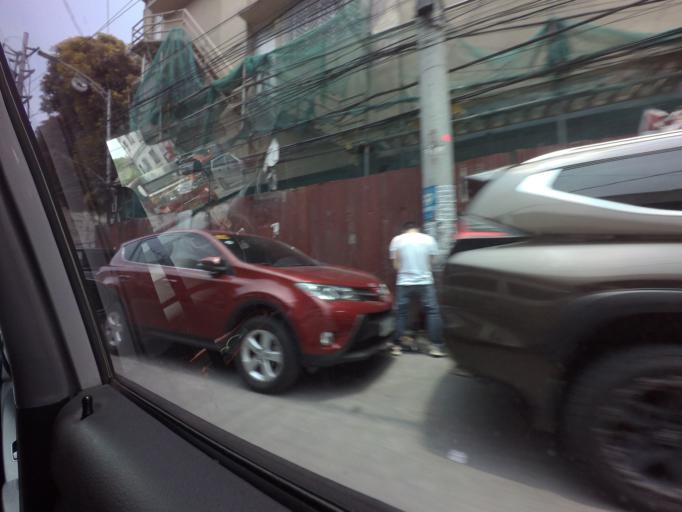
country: PH
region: Metro Manila
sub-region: City of Manila
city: Quiapo
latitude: 14.5960
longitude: 120.9835
